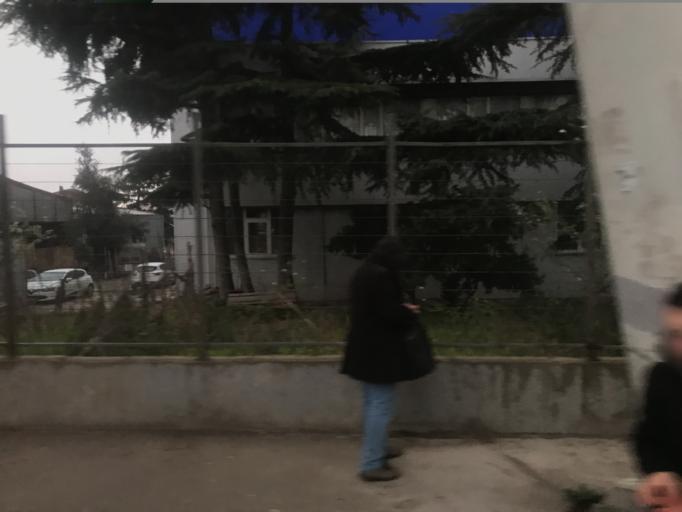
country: TR
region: Istanbul
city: Pendik
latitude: 40.8924
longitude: 29.2319
